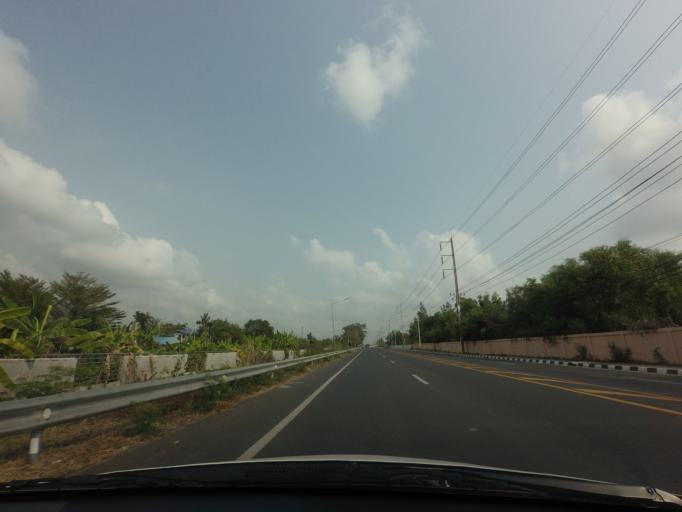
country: TH
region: Pathum Thani
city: Thanyaburi
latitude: 14.0177
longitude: 100.7102
